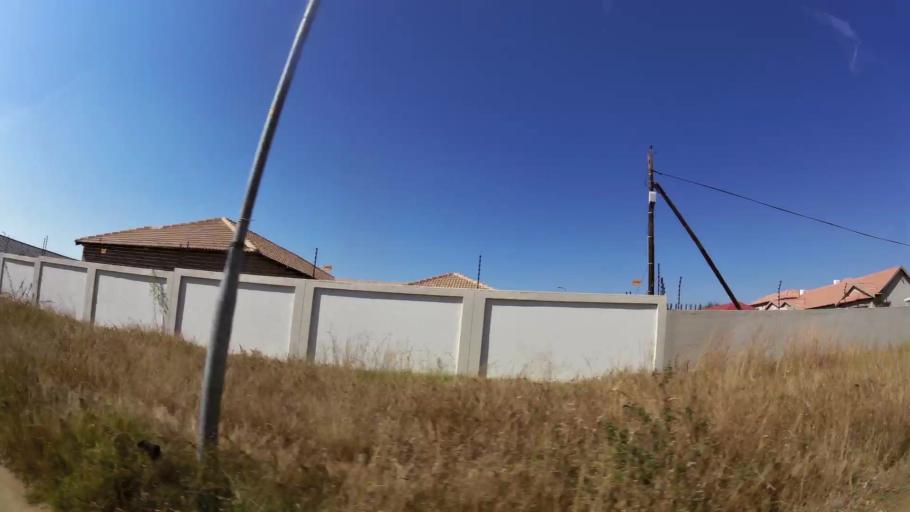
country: ZA
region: Gauteng
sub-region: City of Tshwane Metropolitan Municipality
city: Pretoria
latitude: -25.6511
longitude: 28.2631
